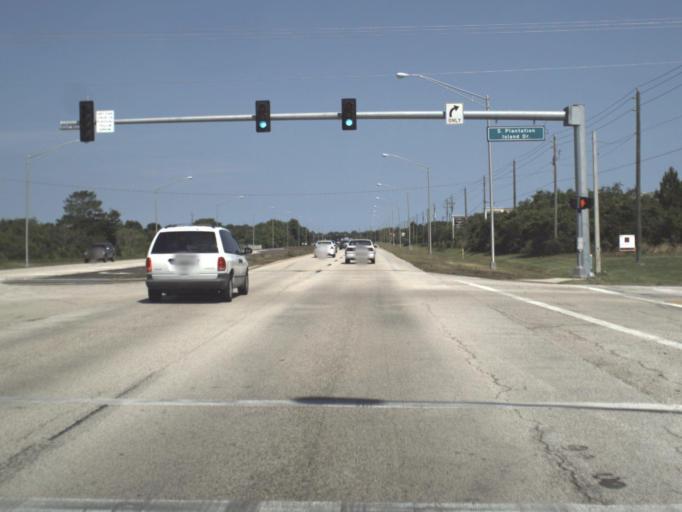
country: US
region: Florida
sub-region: Saint Johns County
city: Saint Augustine South
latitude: 29.8655
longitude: -81.2976
